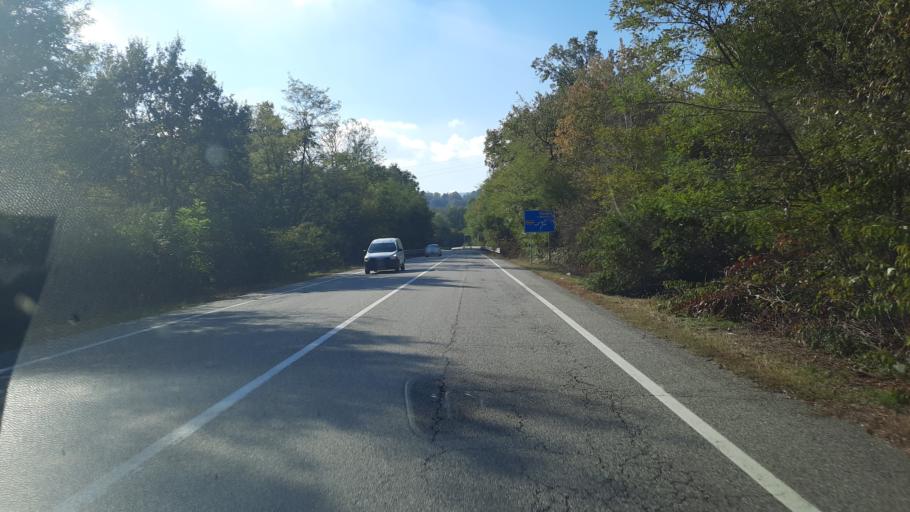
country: IT
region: Piedmont
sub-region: Provincia di Novara
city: Briga Novarese
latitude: 45.7223
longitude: 8.4444
